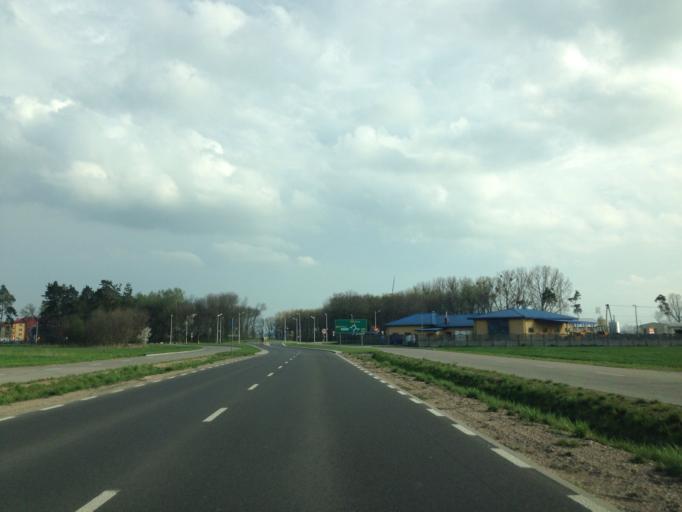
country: PL
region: Masovian Voivodeship
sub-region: Powiat zurominski
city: Zuromin
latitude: 53.0639
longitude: 19.8946
